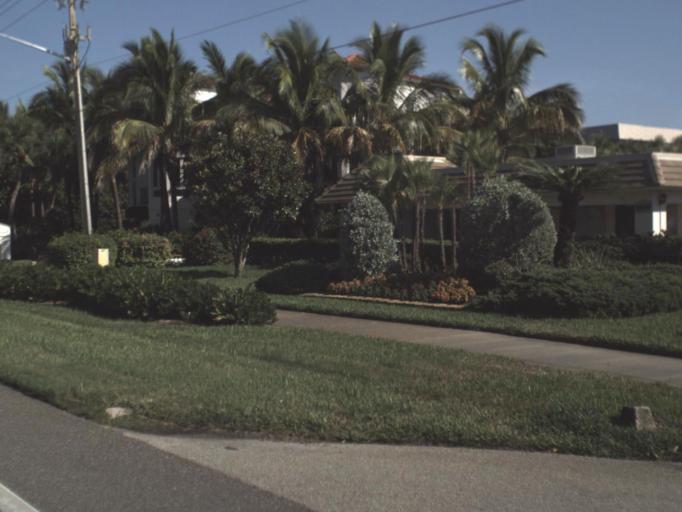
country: US
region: Florida
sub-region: Manatee County
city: Longboat Key
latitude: 27.3751
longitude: -82.6323
